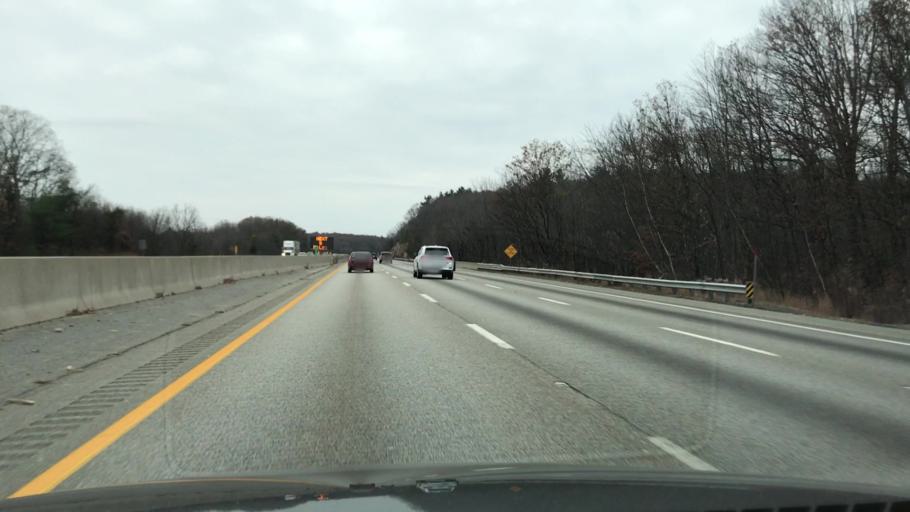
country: US
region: Massachusetts
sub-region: Worcester County
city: Westborough
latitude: 42.2341
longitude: -71.6082
